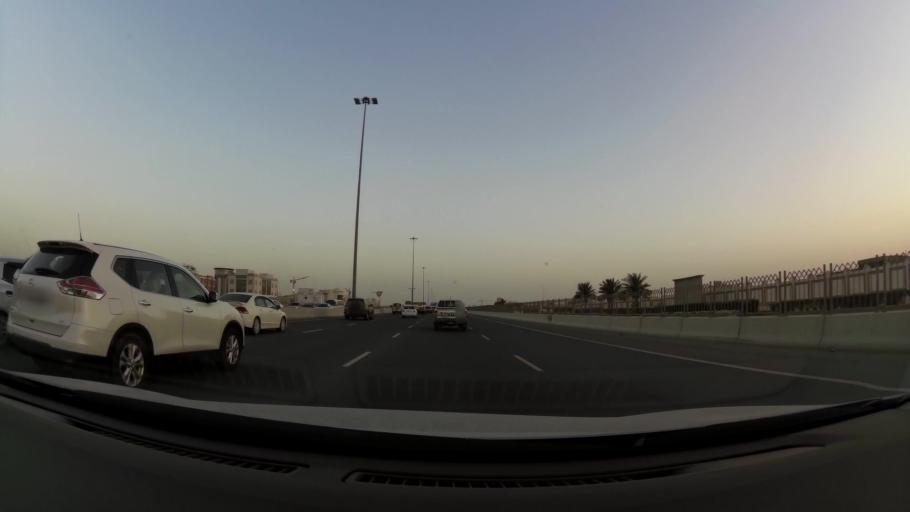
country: QA
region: Baladiyat ar Rayyan
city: Ar Rayyan
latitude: 25.3083
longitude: 51.4724
